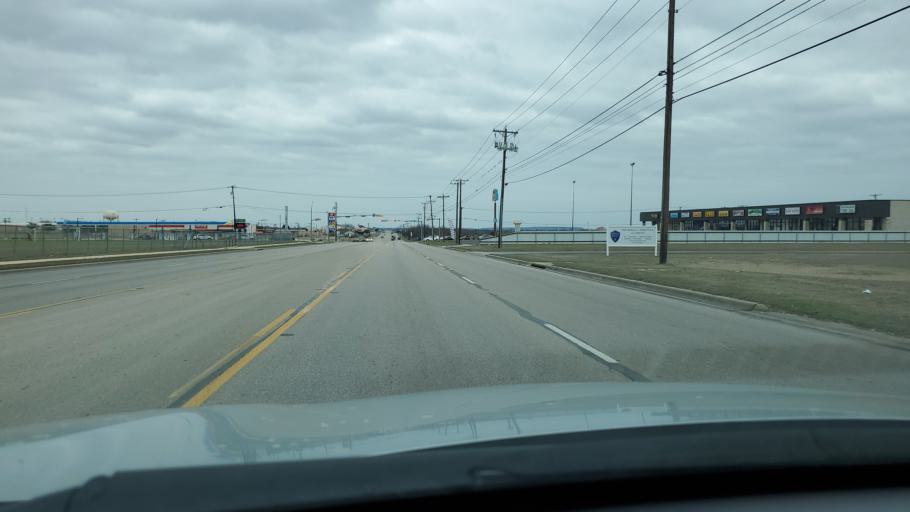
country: US
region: Texas
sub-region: Bell County
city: Killeen
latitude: 31.0816
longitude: -97.7394
